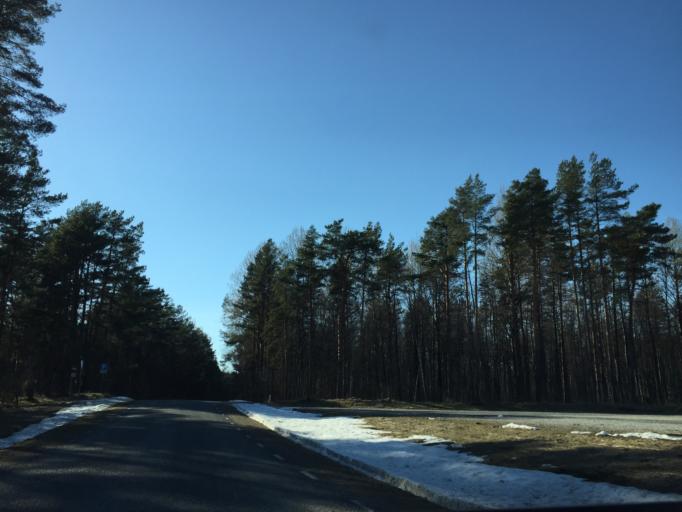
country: RU
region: Pskov
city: Gdov
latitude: 58.9986
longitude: 27.7068
